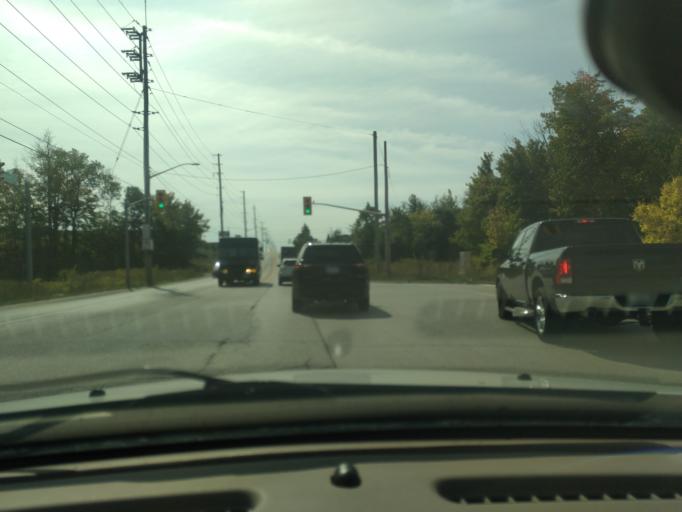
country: CA
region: Ontario
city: Innisfil
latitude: 44.3347
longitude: -79.6783
